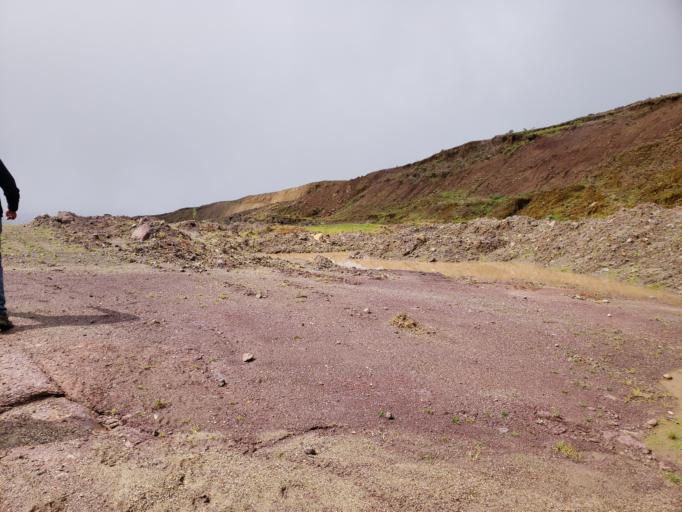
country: ET
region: Oromiya
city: Dodola
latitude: 6.6563
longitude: 39.3628
